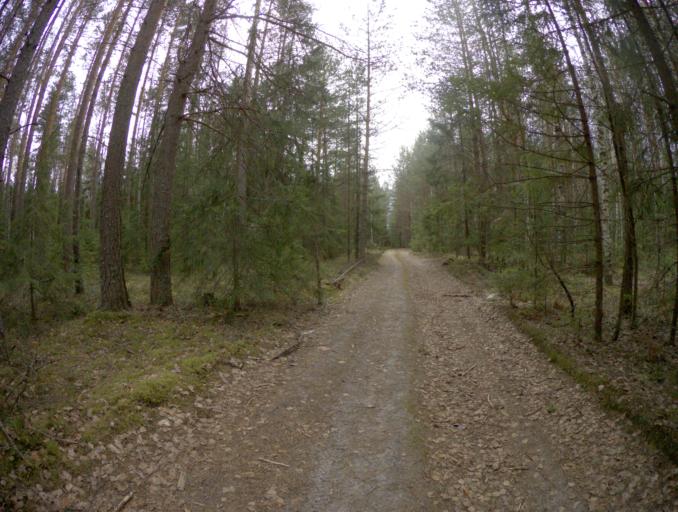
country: RU
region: Vladimir
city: Raduzhnyy
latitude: 55.9487
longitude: 40.2678
